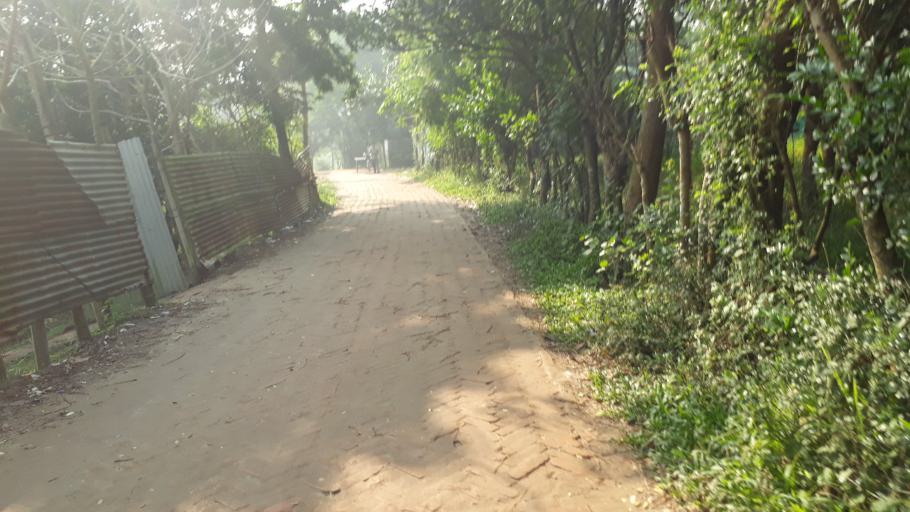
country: BD
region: Dhaka
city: Tungi
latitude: 23.8819
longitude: 90.2581
